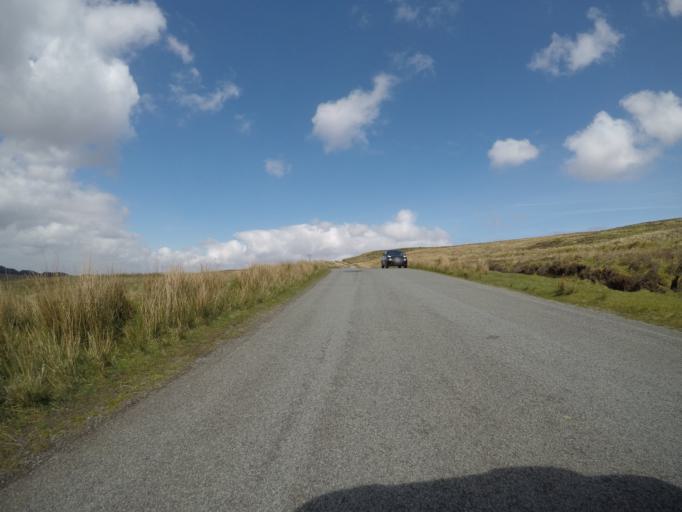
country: GB
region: Scotland
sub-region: Highland
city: Isle of Skye
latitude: 57.4164
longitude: -6.2950
